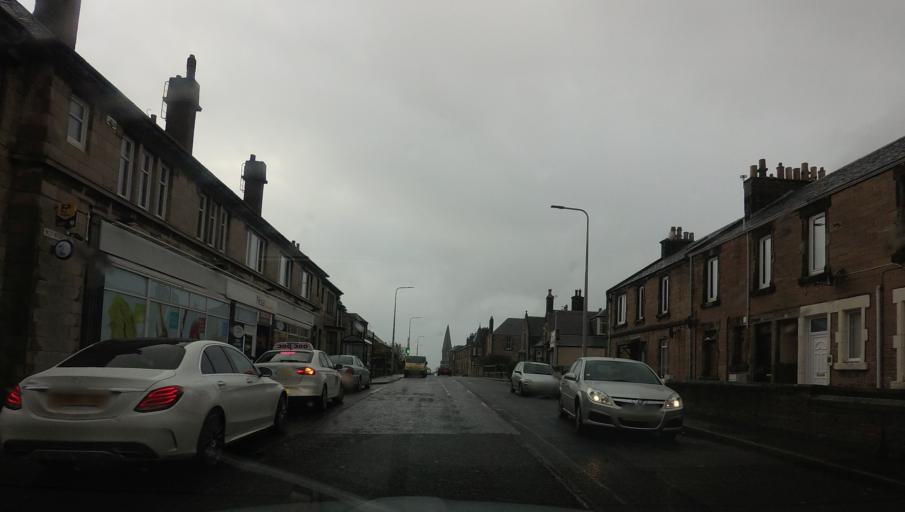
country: GB
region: Scotland
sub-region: Fife
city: Kirkcaldy
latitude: 56.1306
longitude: -3.1214
